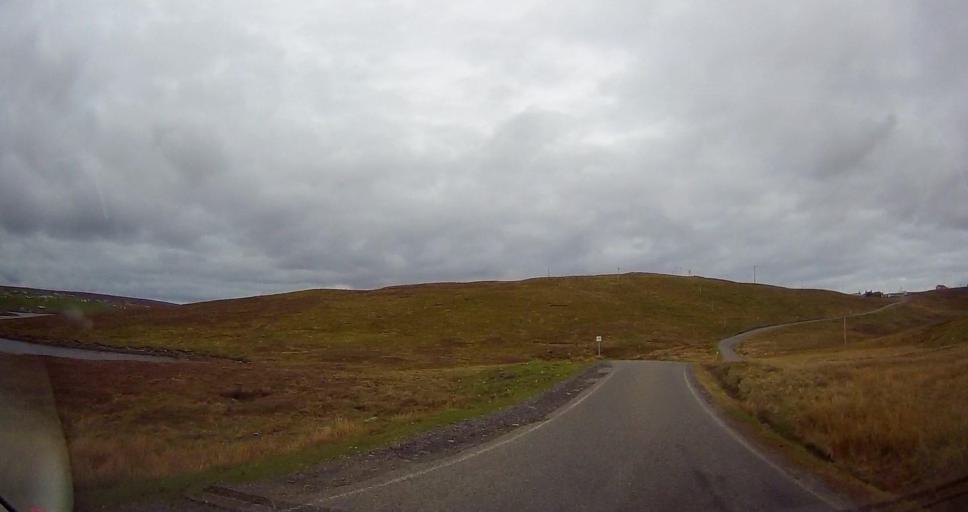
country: GB
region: Scotland
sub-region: Shetland Islands
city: Shetland
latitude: 60.6035
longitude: -1.0858
